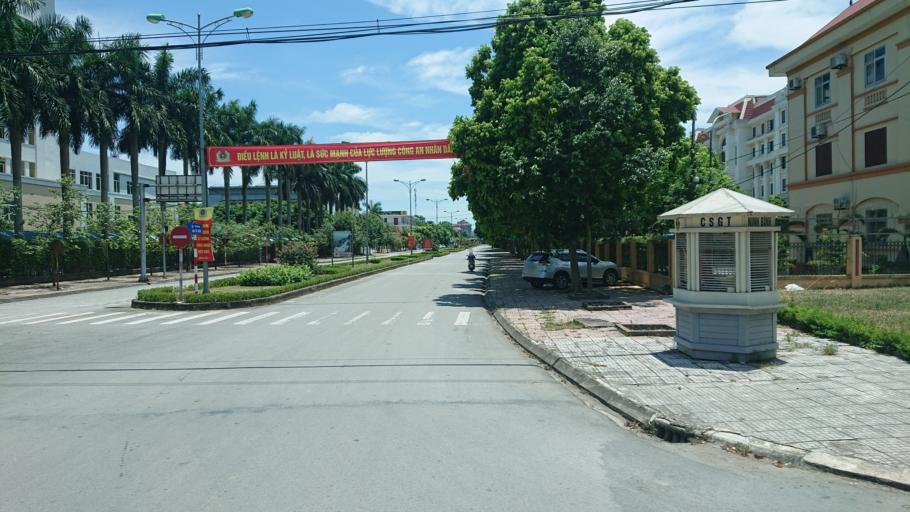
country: VN
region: Ninh Binh
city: Thanh Pho Ninh Binh
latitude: 20.2685
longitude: 105.9722
